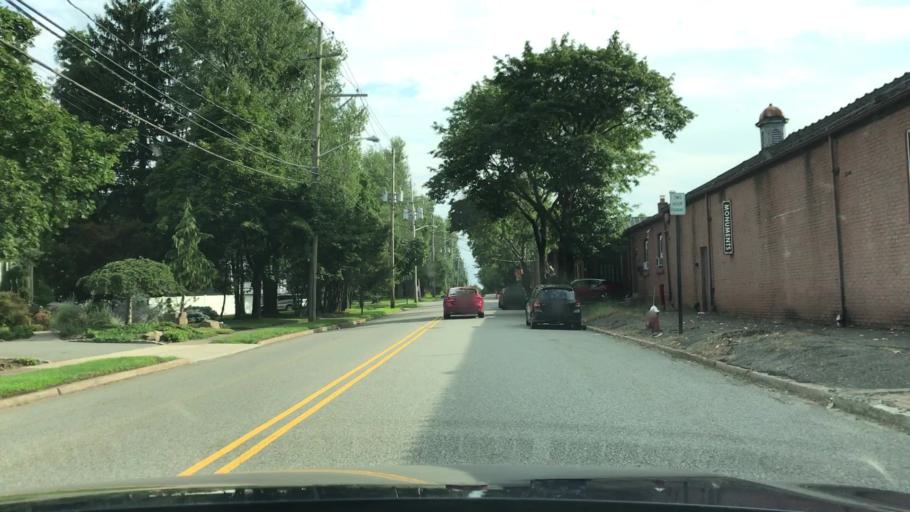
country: US
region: New Jersey
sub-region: Bergen County
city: Closter
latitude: 40.9809
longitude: -73.9582
